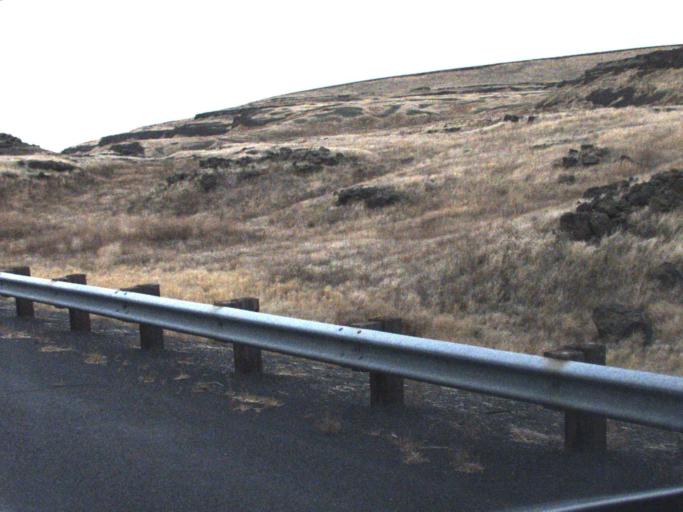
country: US
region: Washington
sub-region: Adams County
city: Ritzville
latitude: 46.7577
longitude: -118.1717
